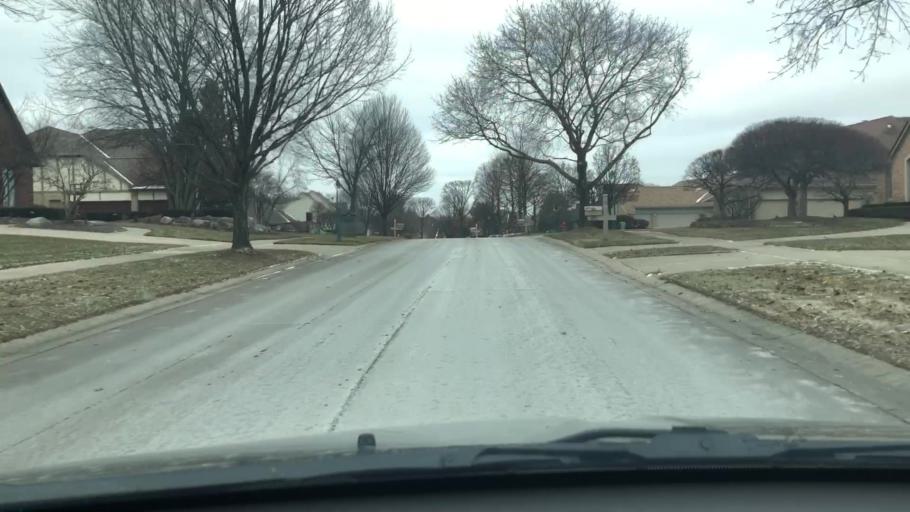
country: US
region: Michigan
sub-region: Oakland County
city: Rochester
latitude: 42.6905
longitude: -83.1150
